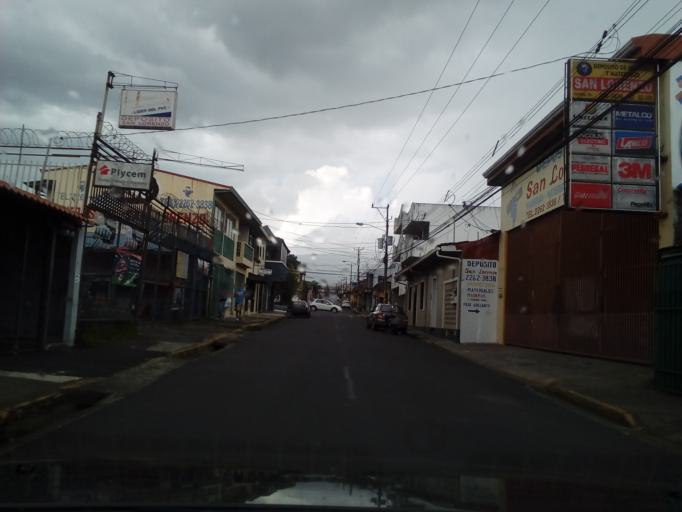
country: CR
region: Heredia
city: Heredia
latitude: 9.9953
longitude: -84.1142
